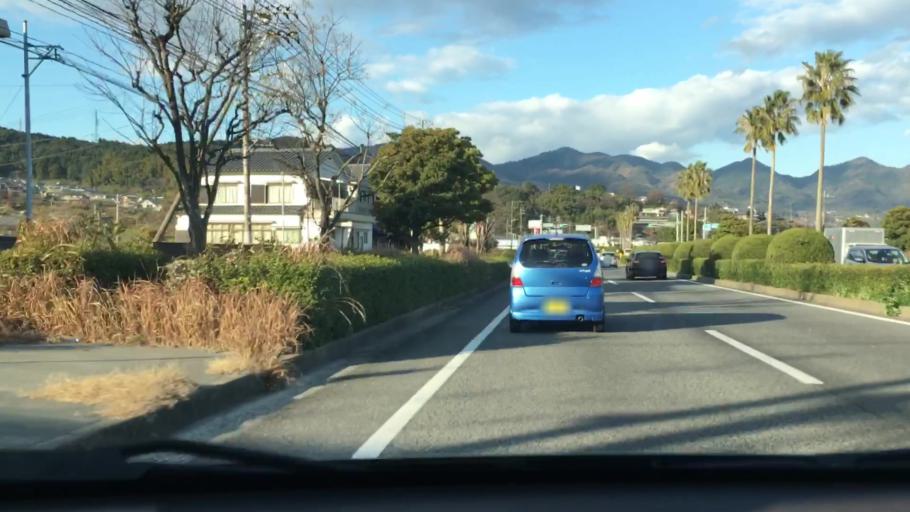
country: JP
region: Oita
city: Hiji
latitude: 33.3408
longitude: 131.4943
